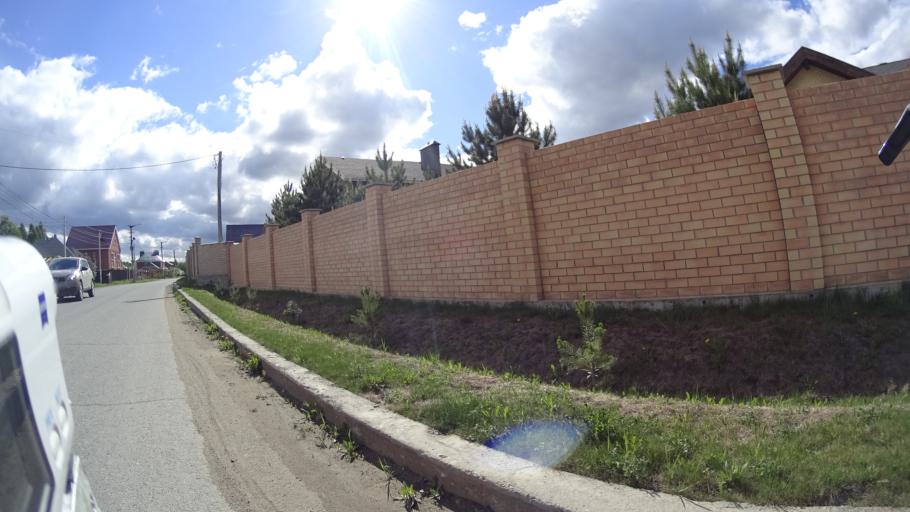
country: RU
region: Chelyabinsk
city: Sargazy
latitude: 55.1473
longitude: 61.2368
